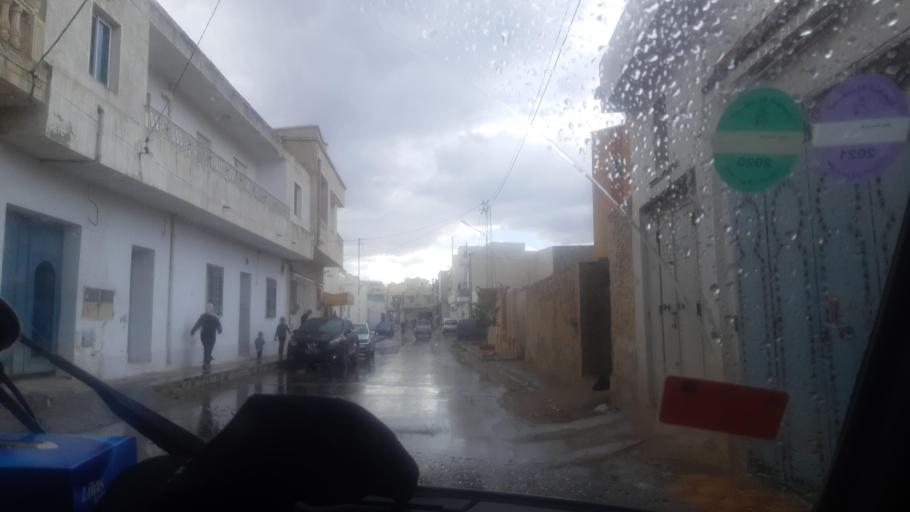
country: TN
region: Susah
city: Akouda
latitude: 35.8719
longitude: 10.5299
